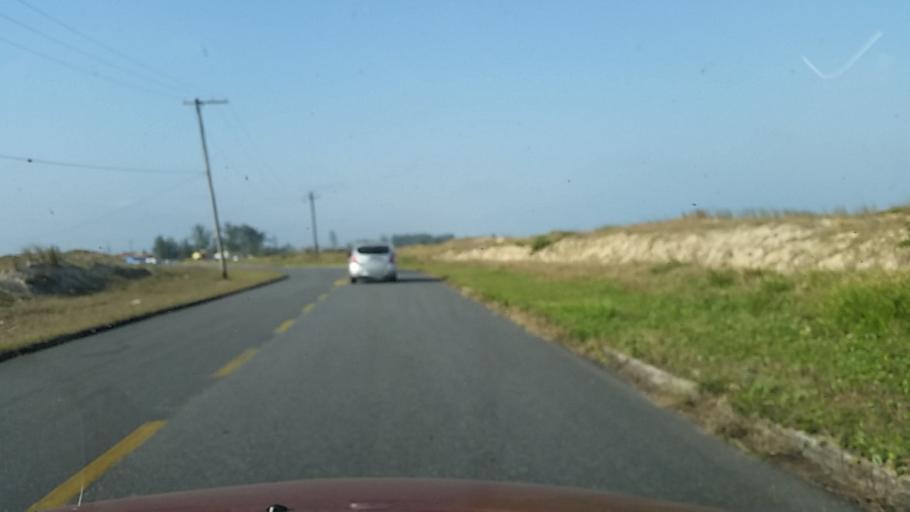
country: BR
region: Sao Paulo
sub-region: Iguape
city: Iguape
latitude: -24.8061
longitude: -47.6365
